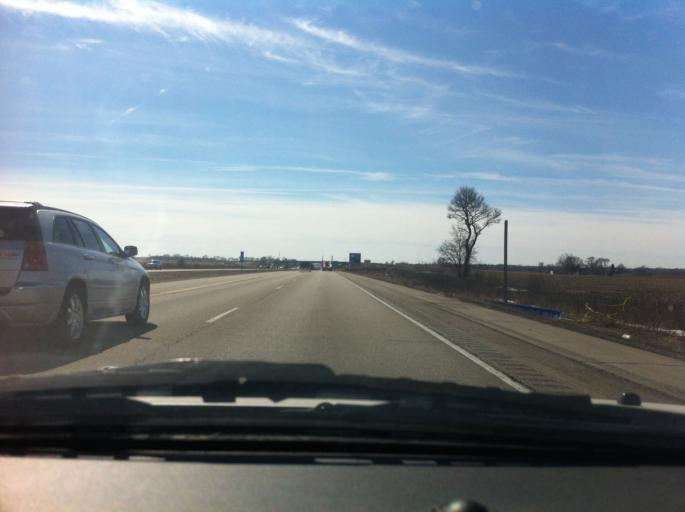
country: US
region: Wisconsin
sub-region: Rock County
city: Janesville
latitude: 42.6140
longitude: -88.9825
